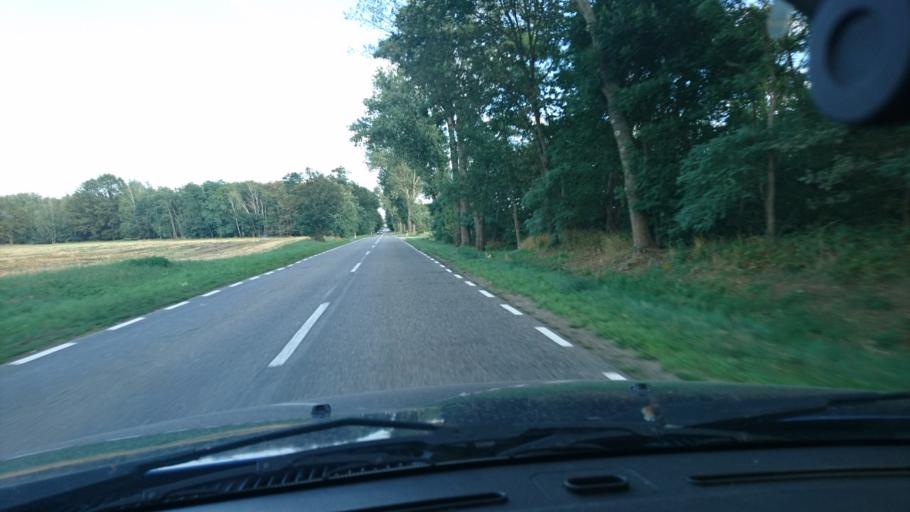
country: PL
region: Greater Poland Voivodeship
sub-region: Powiat ostrowski
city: Odolanow
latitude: 51.5937
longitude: 17.6243
